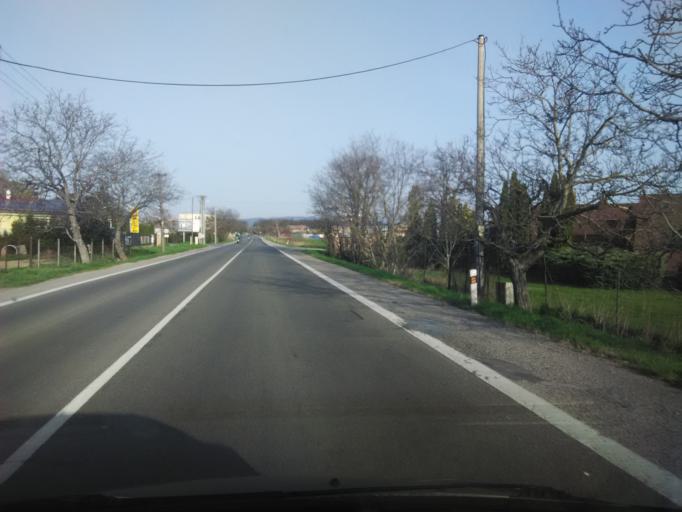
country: SK
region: Bratislavsky
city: Senec
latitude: 48.2016
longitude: 17.3146
